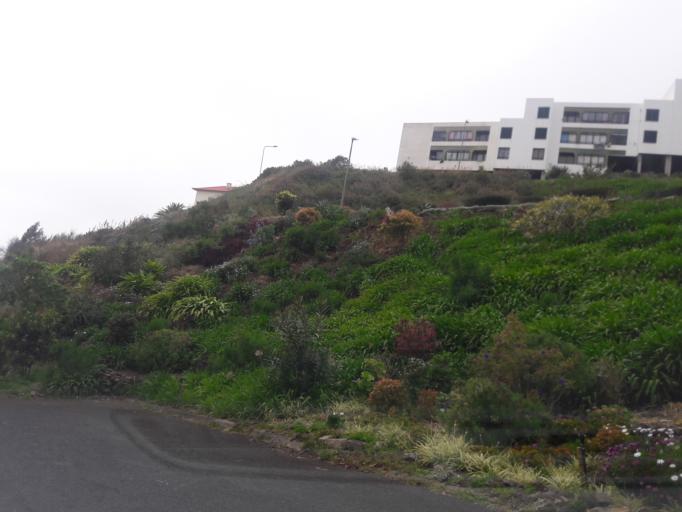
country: PT
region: Madeira
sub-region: Funchal
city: Nossa Senhora do Monte
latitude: 32.6553
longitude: -16.8736
